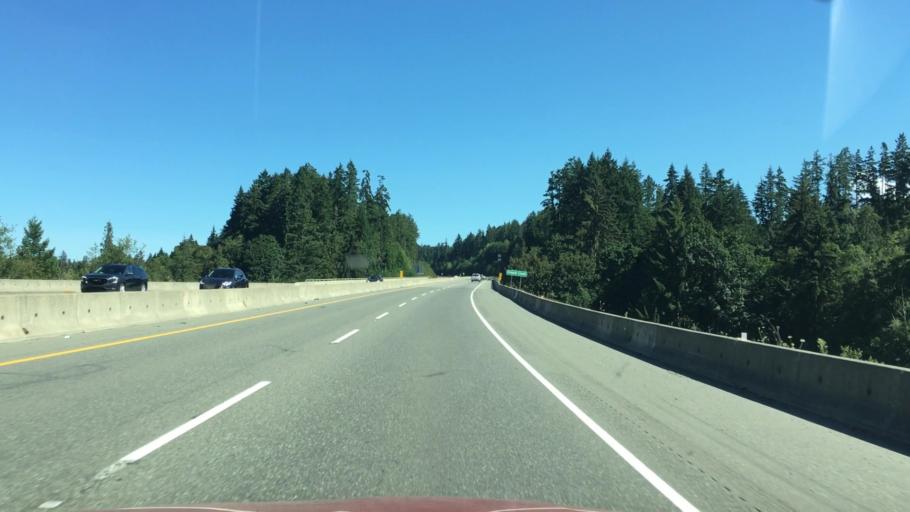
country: CA
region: British Columbia
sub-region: Regional District of Nanaimo
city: Parksville
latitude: 49.3239
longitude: -124.4147
